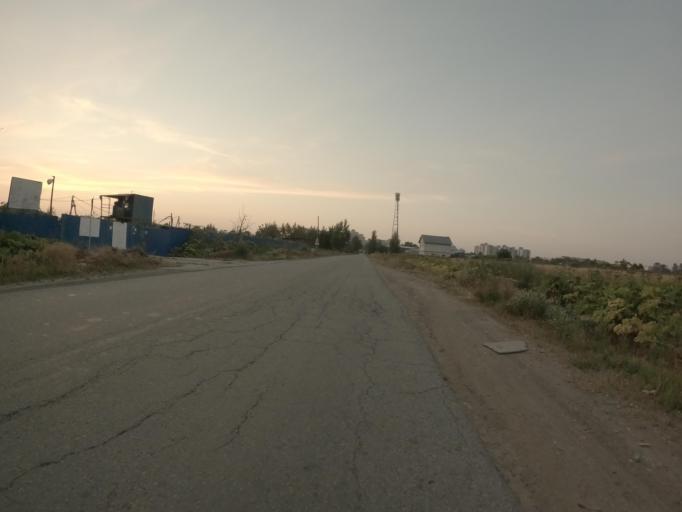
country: RU
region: Leningrad
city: Yanino Vtoroye
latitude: 59.9432
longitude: 30.5538
